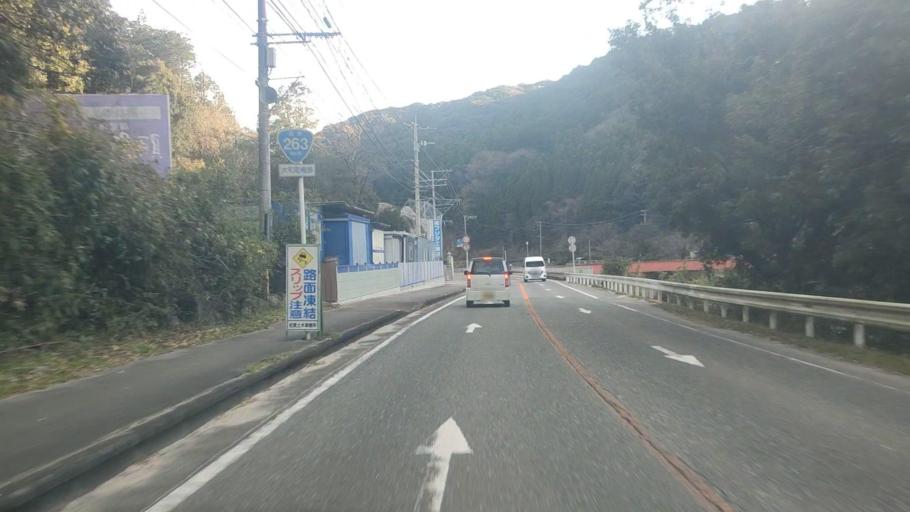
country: JP
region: Saga Prefecture
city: Saga-shi
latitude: 33.3340
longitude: 130.2626
